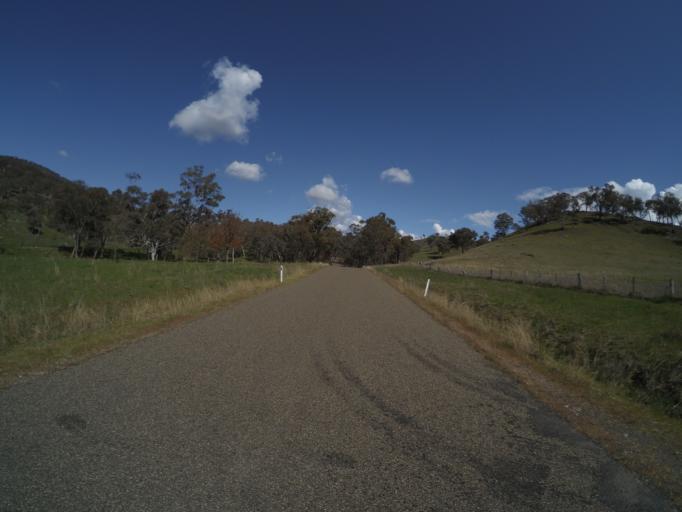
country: AU
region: New South Wales
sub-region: Yass Valley
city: Murrumbateman
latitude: -35.0560
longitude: 148.8390
